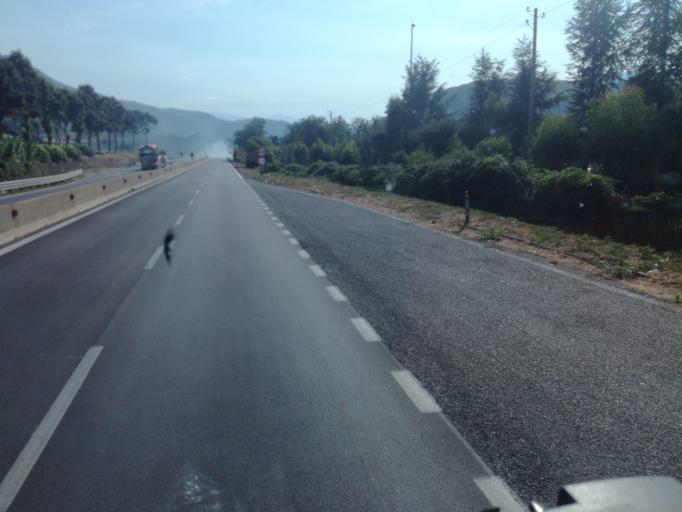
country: IT
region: Campania
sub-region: Provincia di Avellino
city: Torchiati
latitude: 40.8298
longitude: 14.8172
